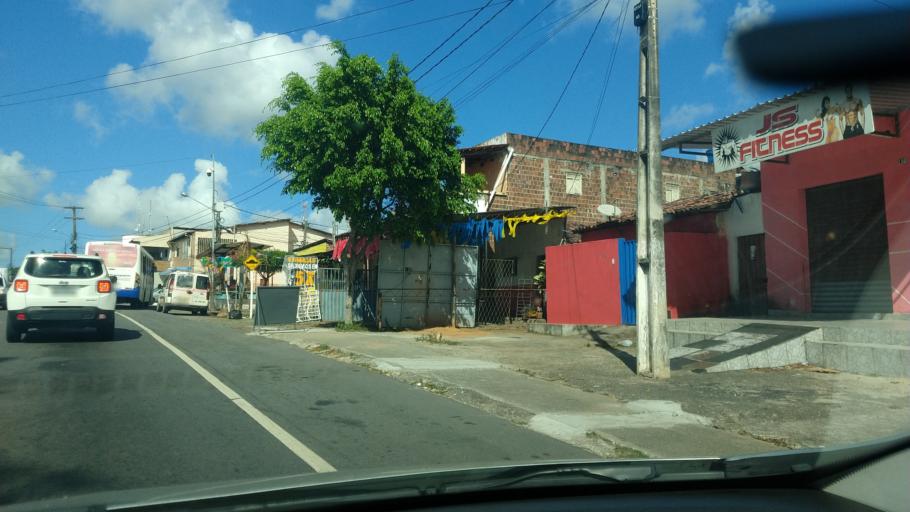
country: BR
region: Rio Grande do Norte
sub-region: Sao Goncalo Do Amarante
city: Sao Goncalo do Amarante
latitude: -5.7896
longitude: -35.3089
